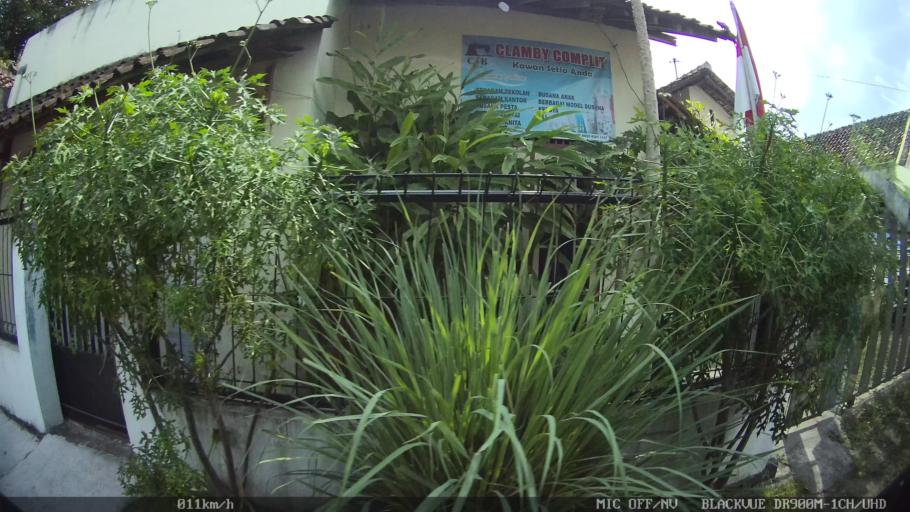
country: ID
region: Daerah Istimewa Yogyakarta
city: Depok
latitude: -7.7959
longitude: 110.4034
